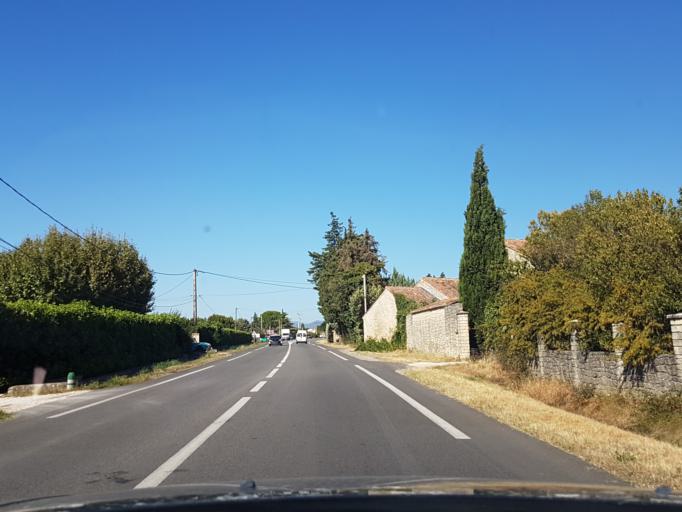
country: FR
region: Provence-Alpes-Cote d'Azur
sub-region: Departement du Vaucluse
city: Pernes-les-Fontaines
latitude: 44.0157
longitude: 5.0300
